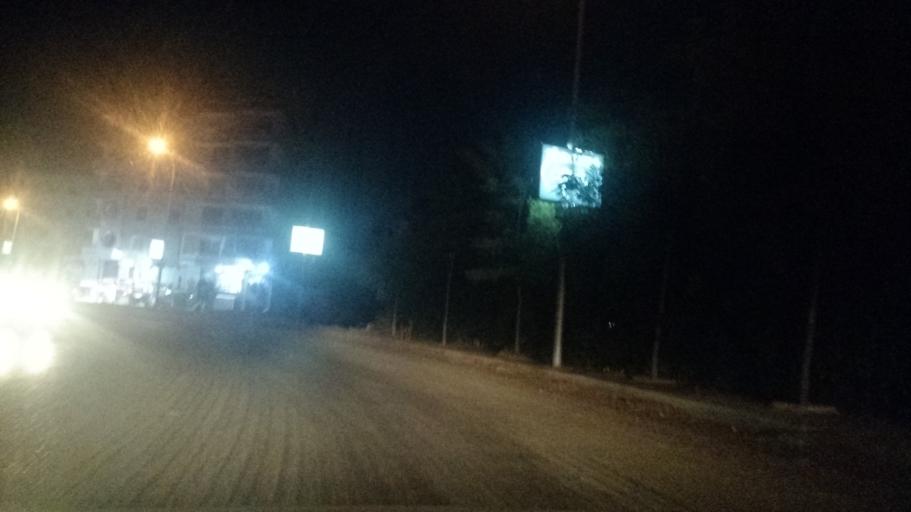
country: EG
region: Muhafazat al Qahirah
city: Cairo
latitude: 30.0070
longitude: 31.2836
